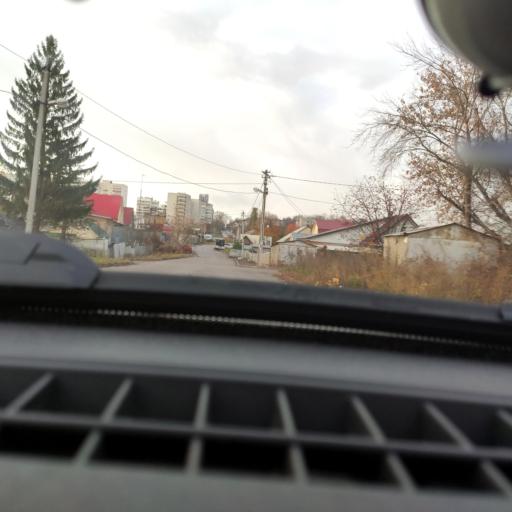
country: RU
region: Bashkortostan
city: Ufa
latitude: 54.8240
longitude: 56.1189
